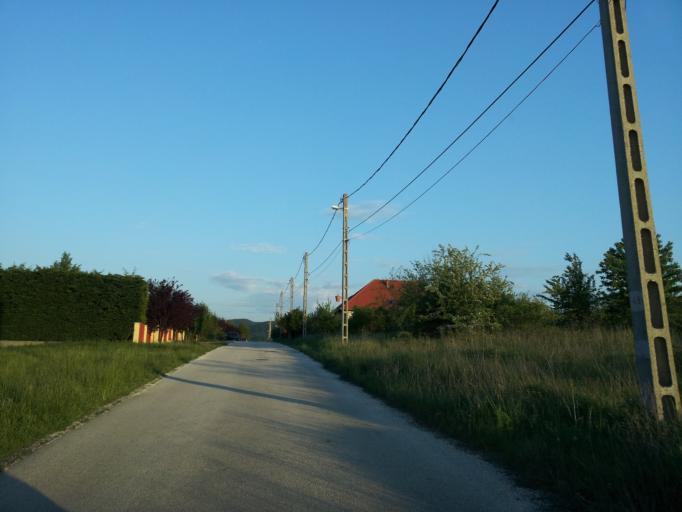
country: HU
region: Pest
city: Piliscsaba
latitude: 47.6241
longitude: 18.8167
